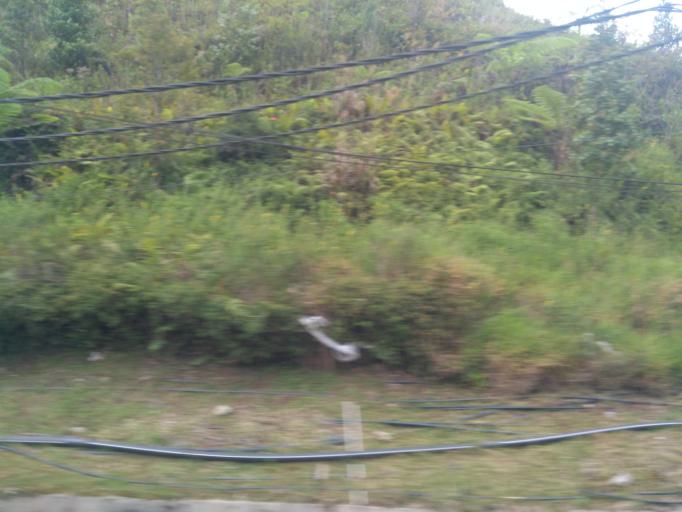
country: MY
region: Pahang
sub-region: Cameron Highlands
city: Tanah Rata
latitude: 4.5724
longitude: 101.4159
